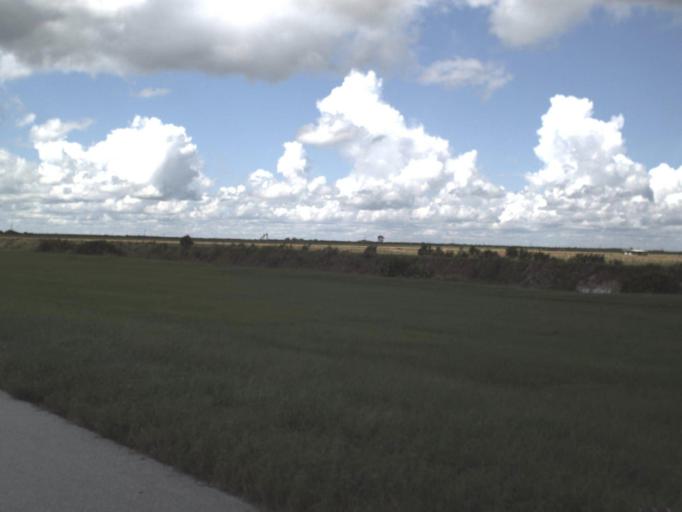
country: US
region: Florida
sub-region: Highlands County
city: Placid Lakes
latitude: 27.2097
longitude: -81.5719
